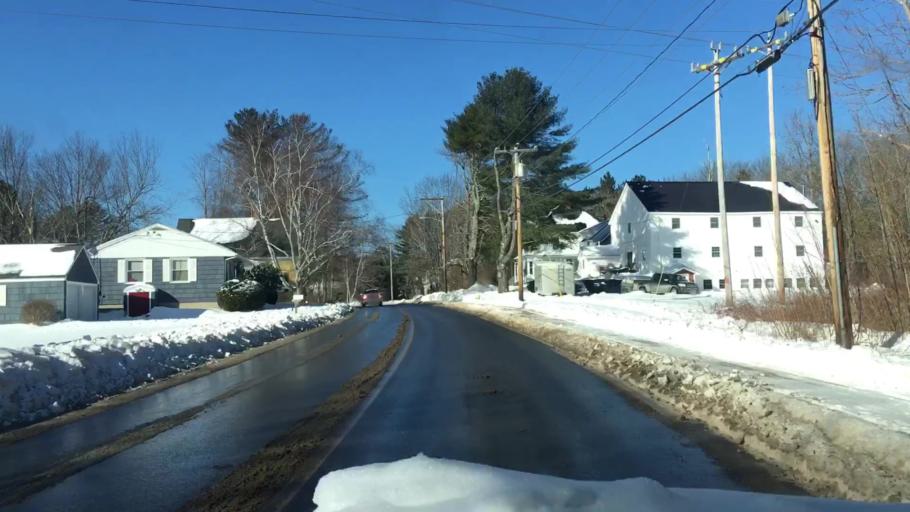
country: US
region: Maine
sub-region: Sagadahoc County
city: Topsham
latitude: 43.9271
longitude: -69.9731
